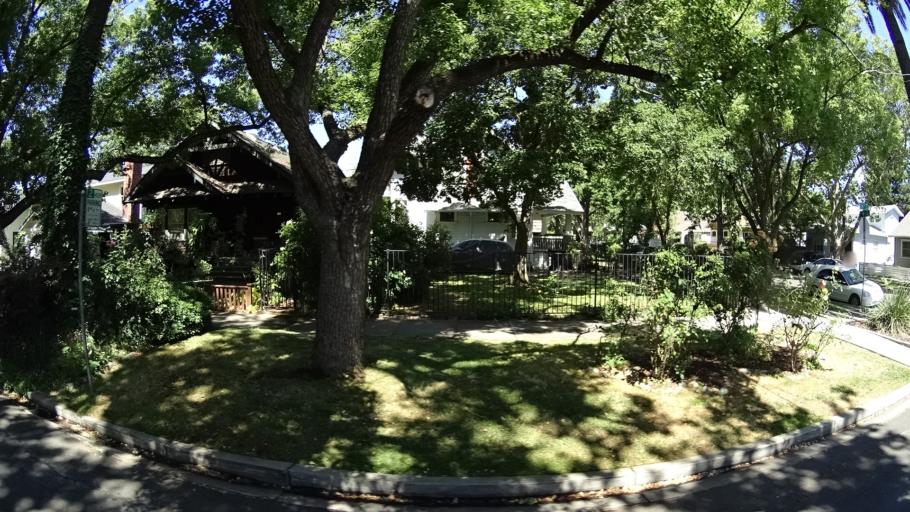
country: US
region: California
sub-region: Sacramento County
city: Sacramento
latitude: 38.5620
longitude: -121.4803
